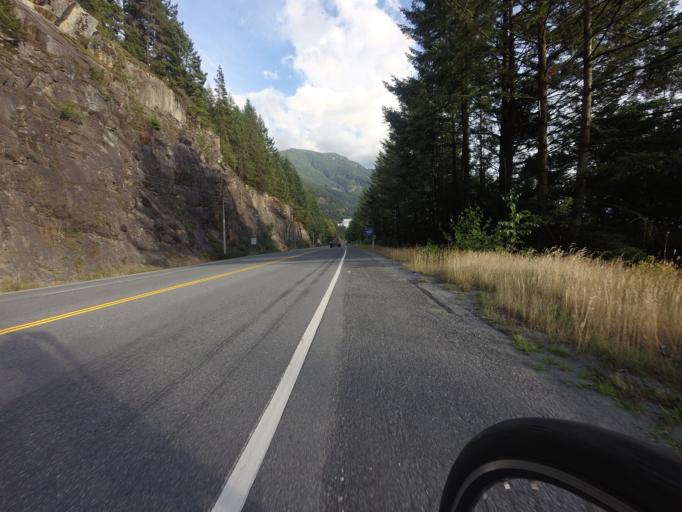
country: CA
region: British Columbia
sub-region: Greater Vancouver Regional District
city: Lions Bay
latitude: 49.6340
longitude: -123.2098
